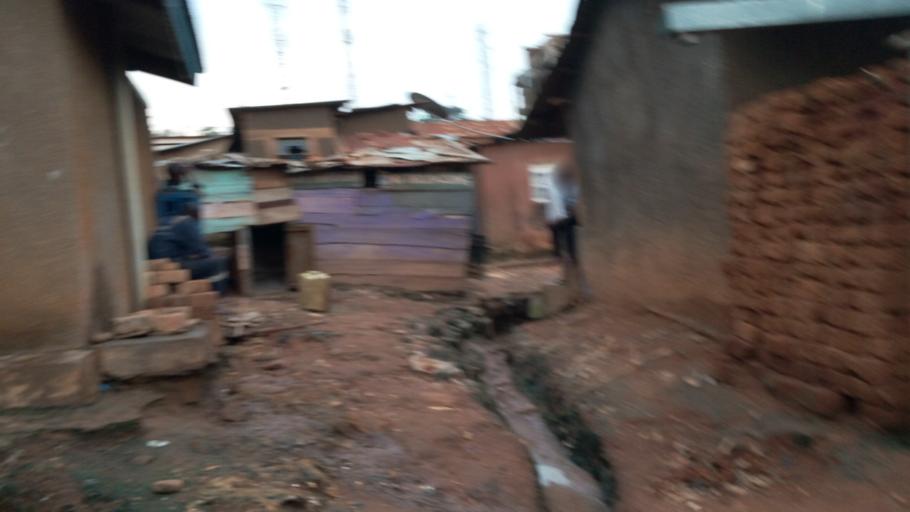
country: UG
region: Central Region
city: Kampala Central Division
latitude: 0.3265
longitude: 32.5685
